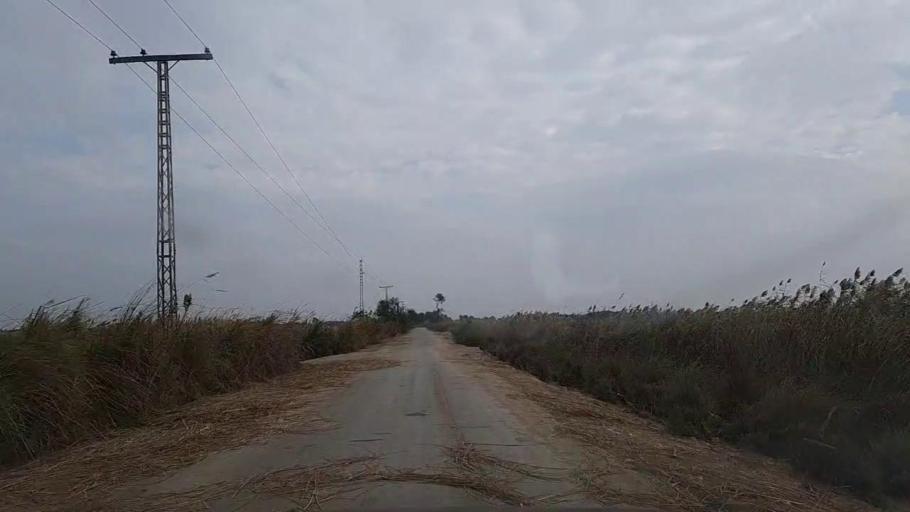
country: PK
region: Sindh
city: Sanghar
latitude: 26.2307
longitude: 68.9882
